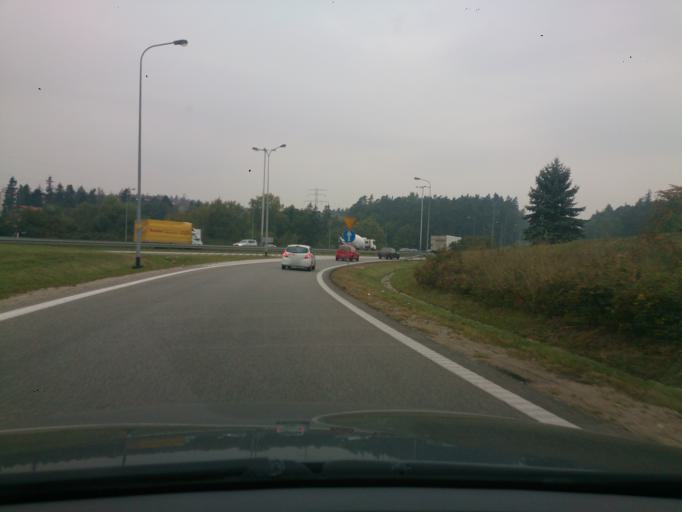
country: PL
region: Pomeranian Voivodeship
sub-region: Sopot
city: Sopot
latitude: 54.3786
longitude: 18.5136
